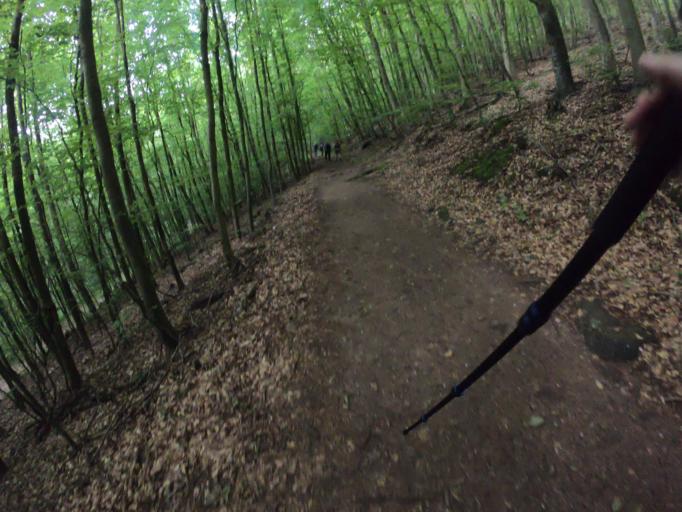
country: DE
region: Rheinland-Pfalz
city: Annweiler am Trifels
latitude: 49.1970
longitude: 7.9814
